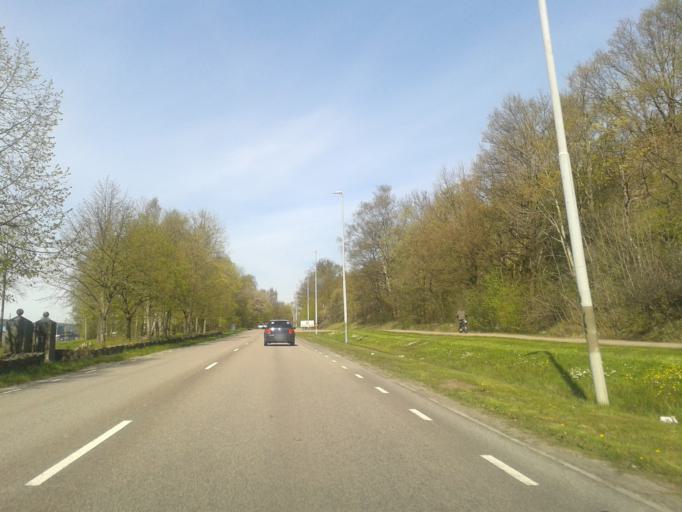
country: SE
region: Vaestra Goetaland
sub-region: Goteborg
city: Eriksbo
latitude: 57.7380
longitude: 12.0058
